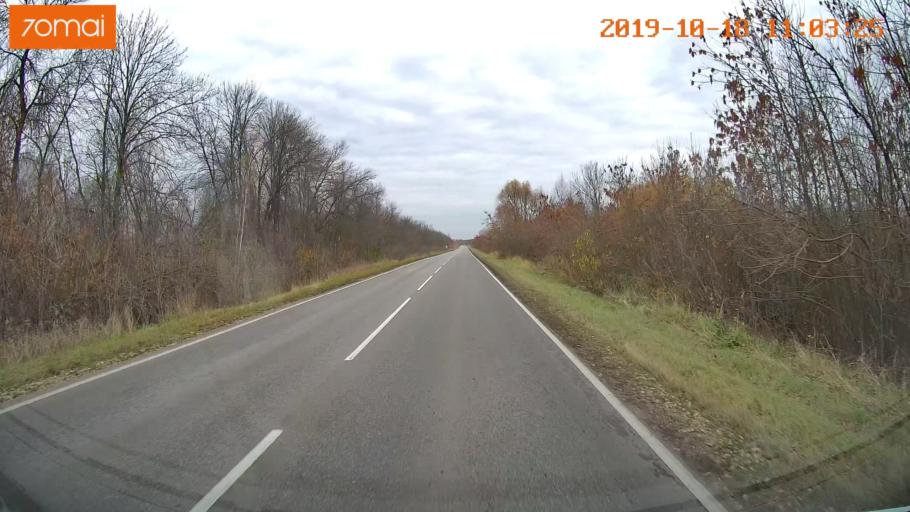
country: RU
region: Tula
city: Yepifan'
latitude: 53.8793
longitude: 38.5485
